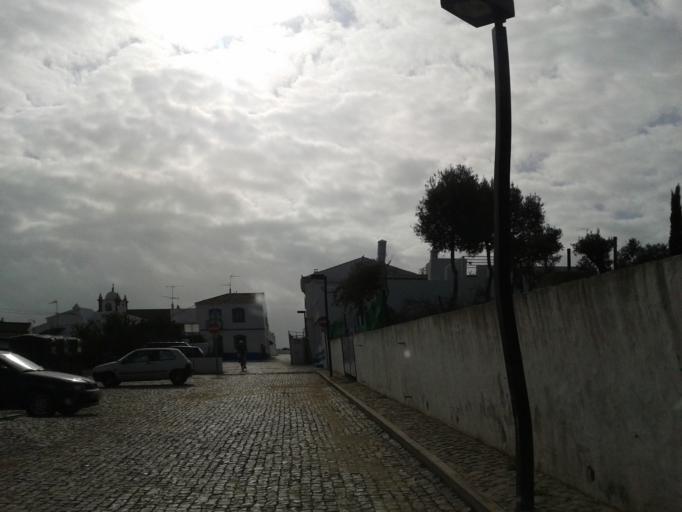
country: PT
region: Faro
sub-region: Vila Real de Santo Antonio
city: Monte Gordo
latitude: 37.1581
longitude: -7.5468
